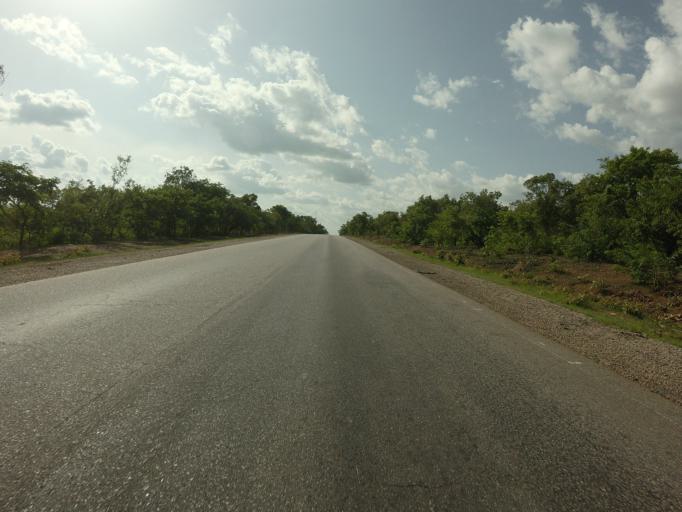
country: GH
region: Upper East
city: Bolgatanga
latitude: 10.5424
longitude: -0.8246
